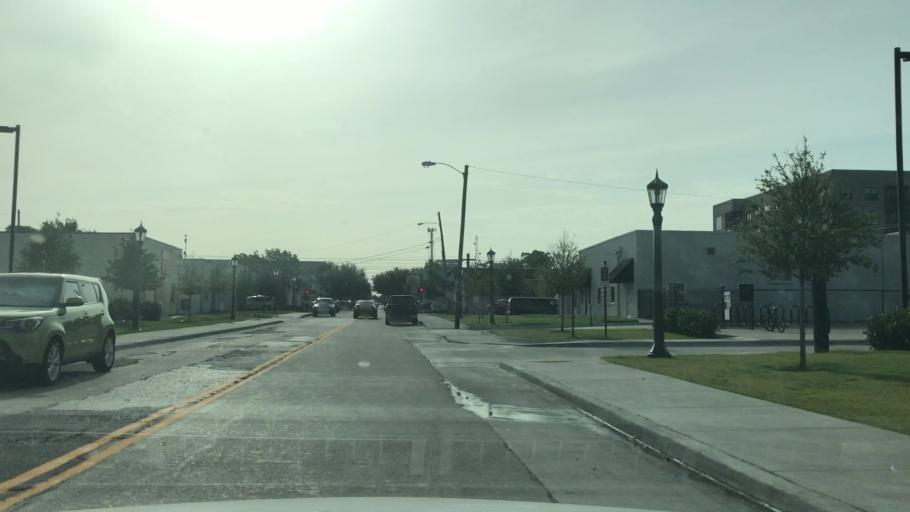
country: US
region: Texas
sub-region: Dallas County
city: Highland Park
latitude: 32.8431
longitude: -96.7738
